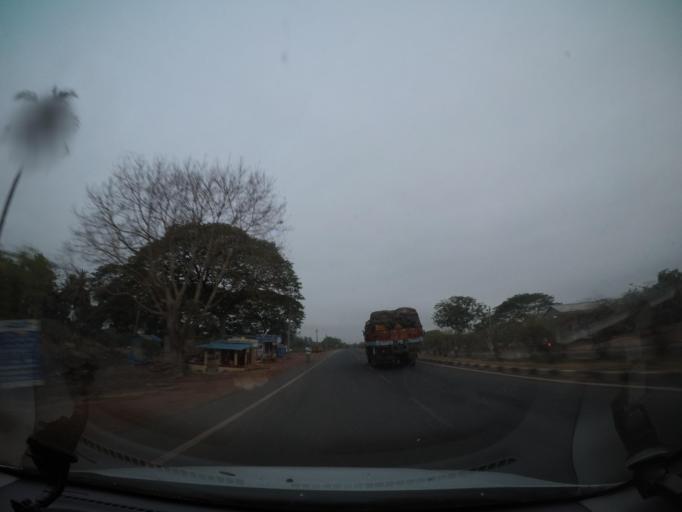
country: IN
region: Andhra Pradesh
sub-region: West Godavari
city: Eluru
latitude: 16.8043
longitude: 81.2987
